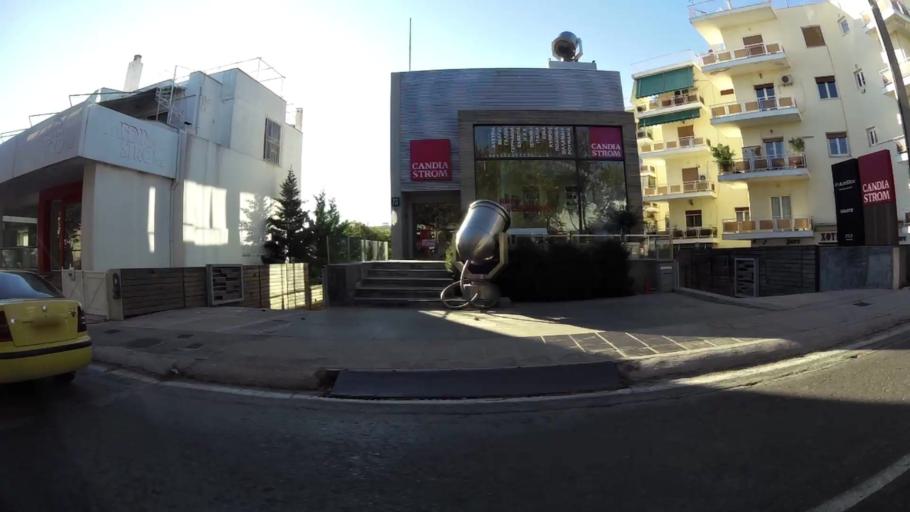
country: GR
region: Attica
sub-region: Nomarchia Athinas
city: Kifisia
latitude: 38.0692
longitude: 23.8110
